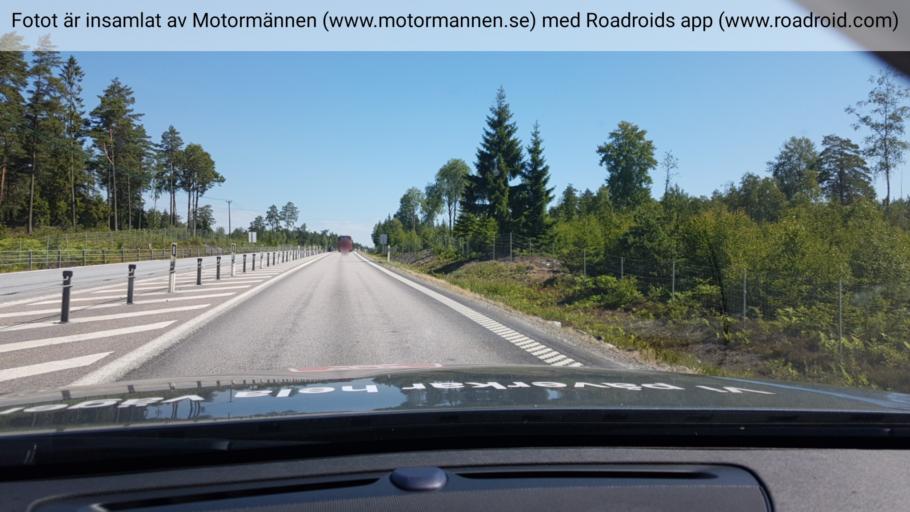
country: SE
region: Stockholm
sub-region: Osterakers Kommun
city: Akersberga
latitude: 59.5790
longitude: 18.2437
